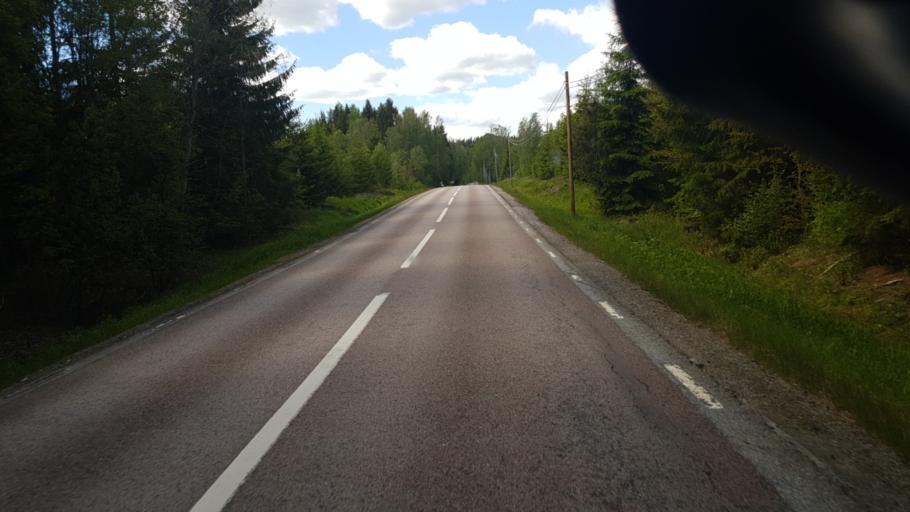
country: SE
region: Vaermland
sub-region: Sunne Kommun
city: Sunne
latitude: 59.6670
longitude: 12.9977
